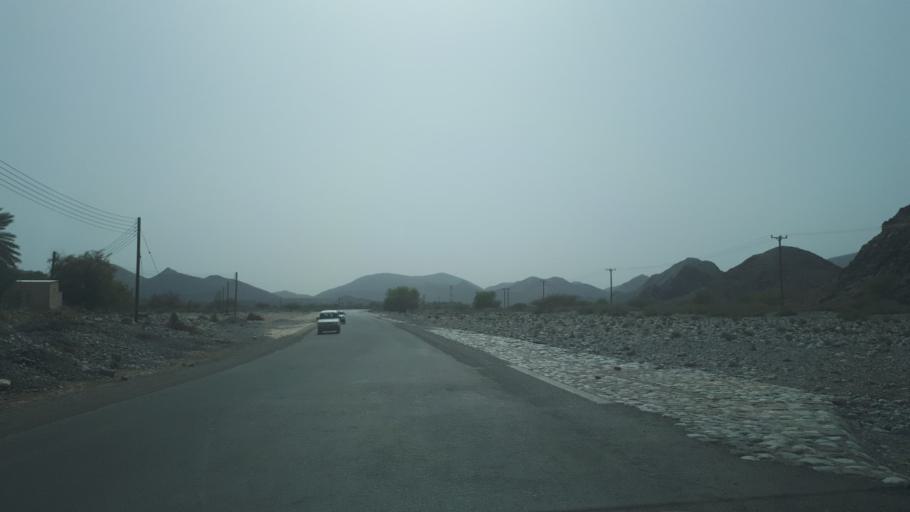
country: OM
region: Muhafazat ad Dakhiliyah
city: Bahla'
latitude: 23.2181
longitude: 57.0099
